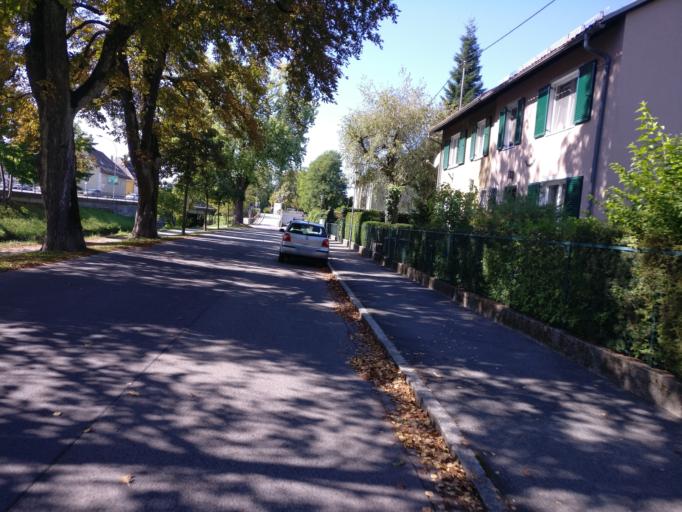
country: AT
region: Carinthia
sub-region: Klagenfurt am Woerthersee
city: Klagenfurt am Woerthersee
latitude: 46.6200
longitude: 14.2725
